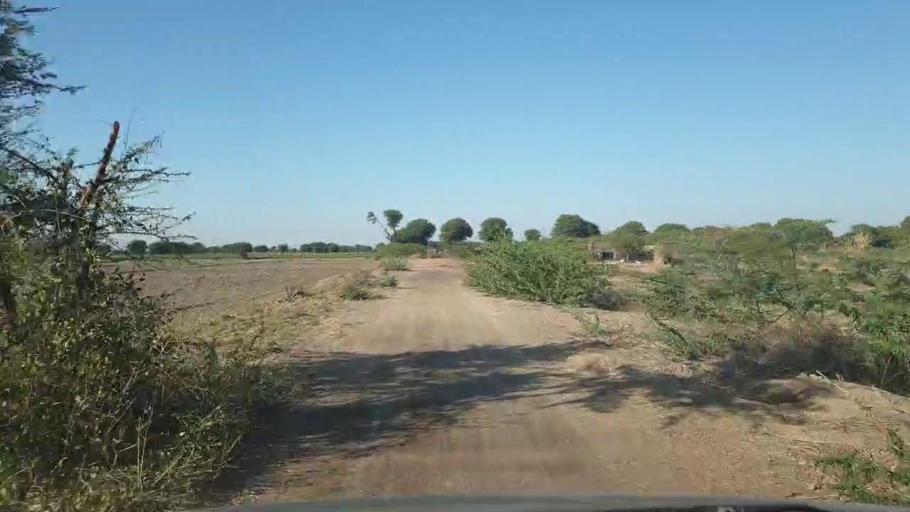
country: PK
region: Sindh
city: Dhoro Naro
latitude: 25.4327
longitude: 69.5438
